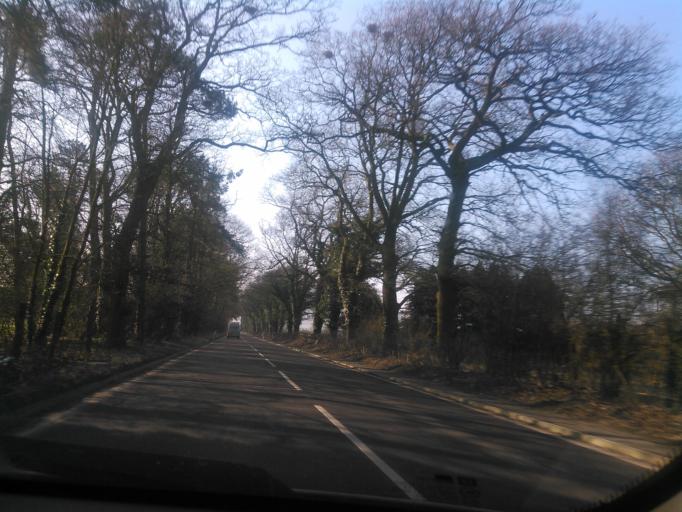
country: GB
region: England
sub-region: Shropshire
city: Craven Arms
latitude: 52.4533
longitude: -2.8374
